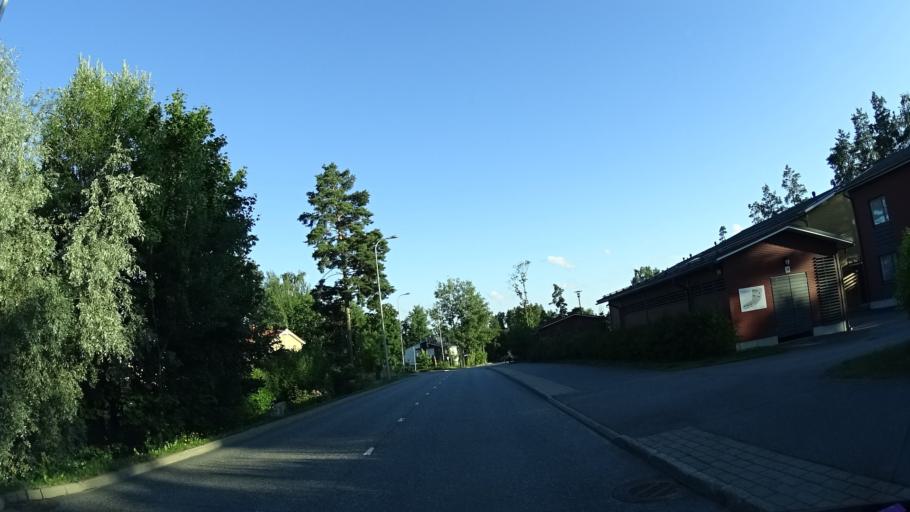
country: FI
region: Uusimaa
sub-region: Helsinki
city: Teekkarikylae
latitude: 60.2857
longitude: 24.8755
